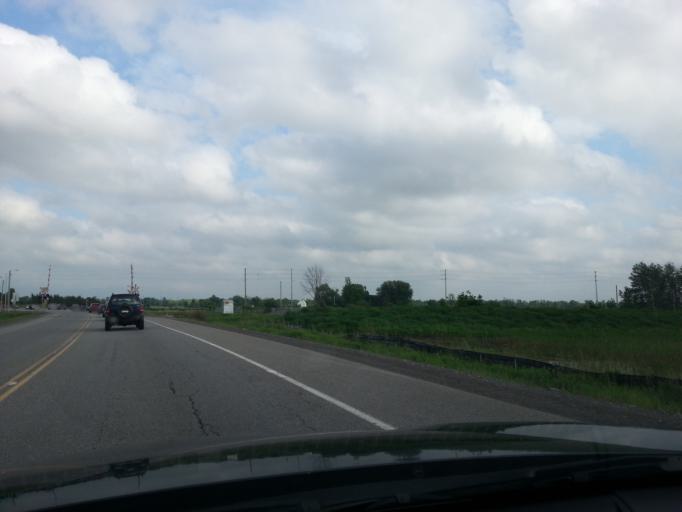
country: CA
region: Ontario
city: Bells Corners
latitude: 45.2612
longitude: -75.7746
